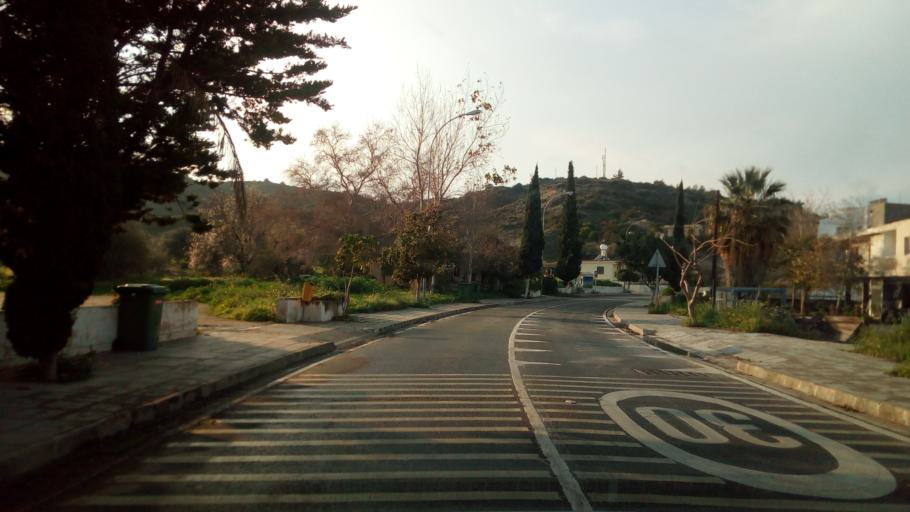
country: CY
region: Lefkosia
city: Kato Pyrgos
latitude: 35.1886
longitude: 32.6710
